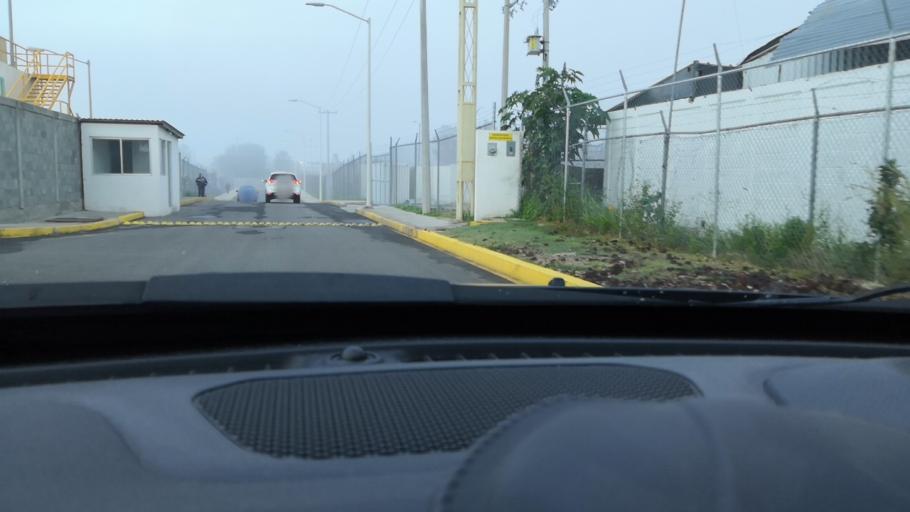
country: MX
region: Guanajuato
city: Colonia Nuevo Mexico
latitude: 20.9866
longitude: -101.4813
